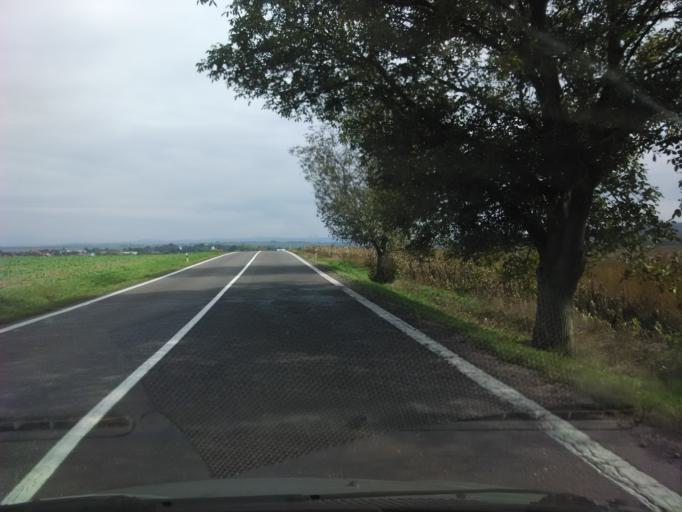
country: SK
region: Nitriansky
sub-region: Okres Nitra
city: Vrable
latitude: 48.2751
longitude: 18.2423
